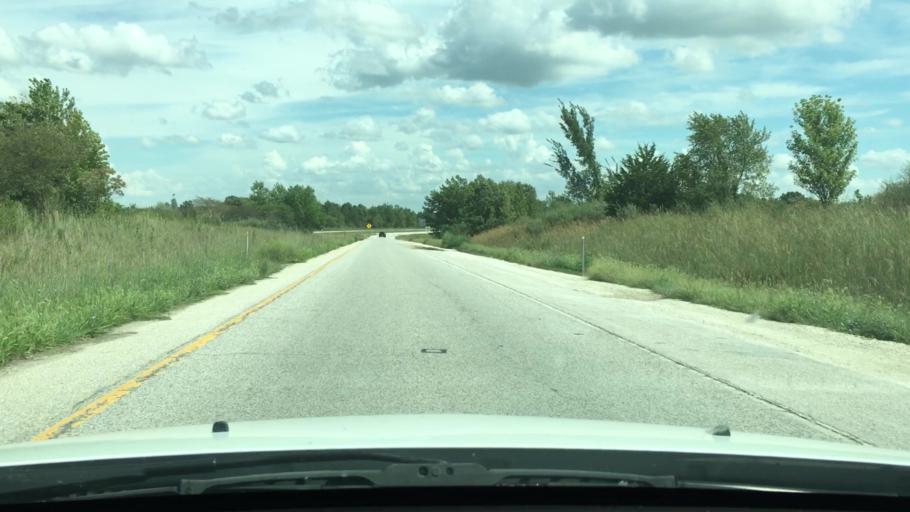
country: US
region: Illinois
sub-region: Pike County
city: Griggsville
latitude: 39.6729
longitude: -90.7680
